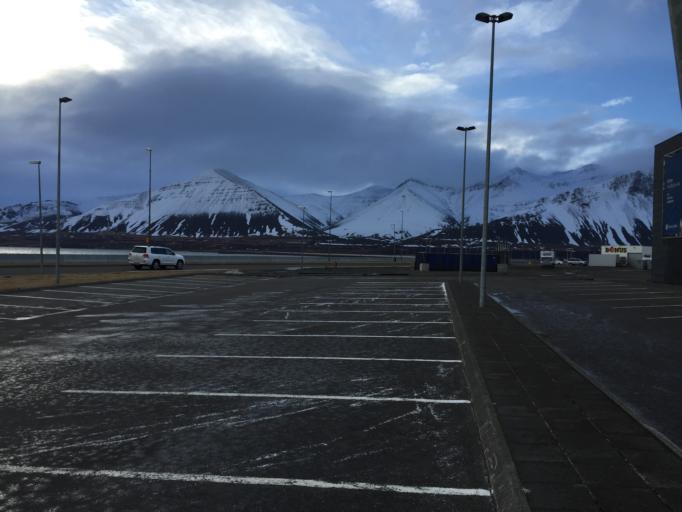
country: IS
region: West
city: Borgarnes
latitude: 64.5430
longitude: -21.9093
